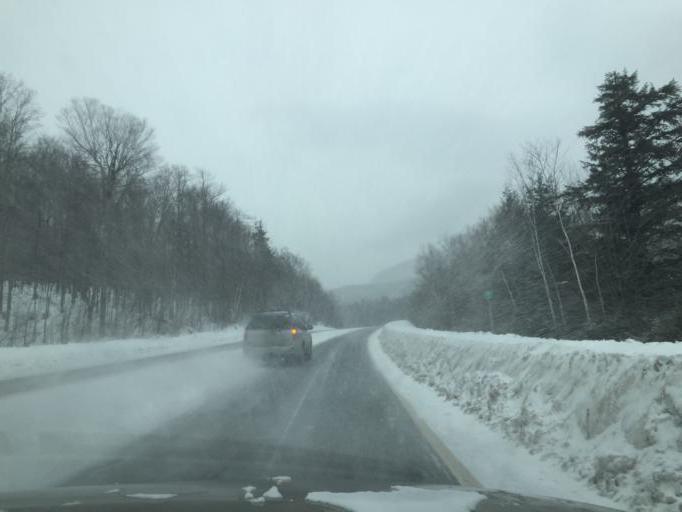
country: US
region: New Hampshire
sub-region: Carroll County
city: North Conway
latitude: 44.2072
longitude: -71.2414
